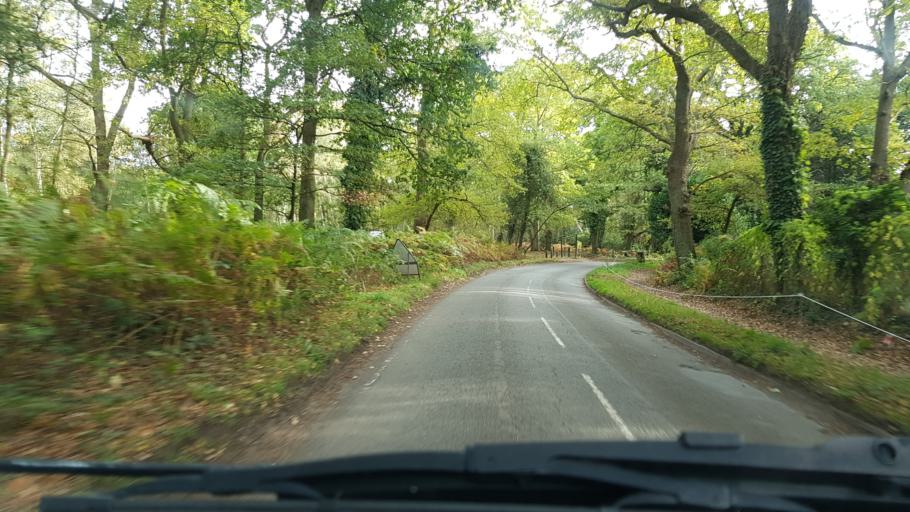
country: GB
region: England
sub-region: Surrey
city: Byfleet
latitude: 51.3201
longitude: -0.4732
